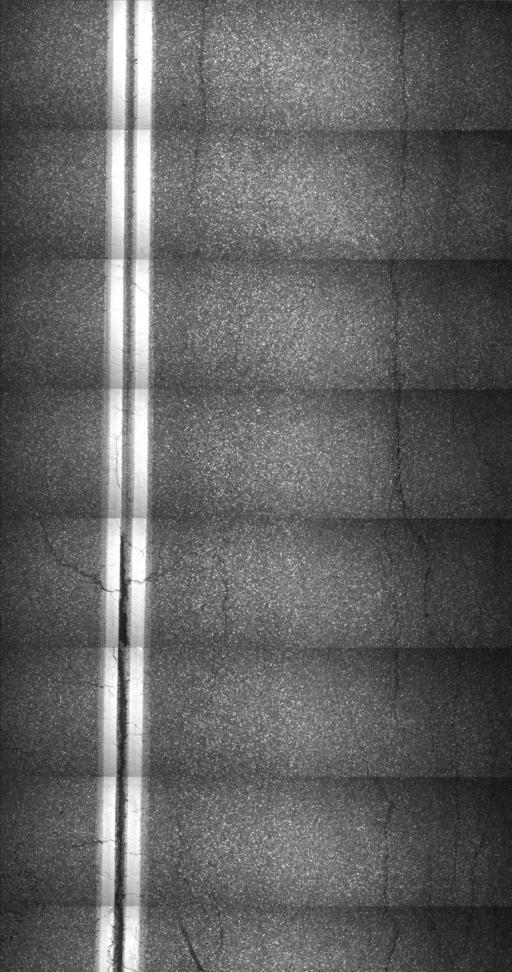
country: US
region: Vermont
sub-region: Chittenden County
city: Williston
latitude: 44.4401
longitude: -73.0198
